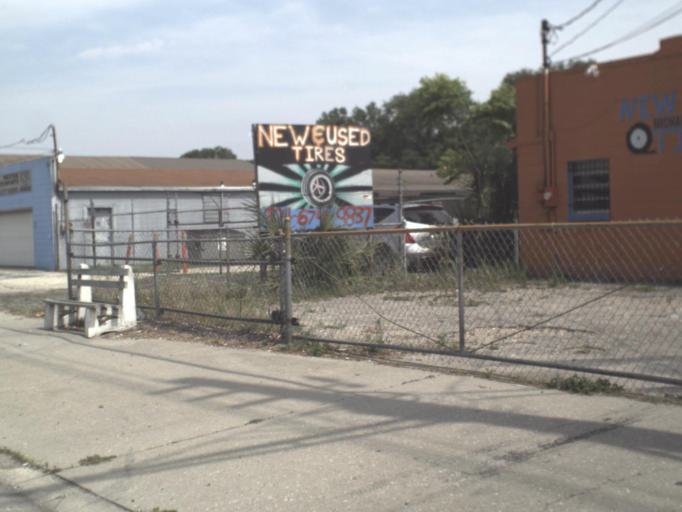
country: US
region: Florida
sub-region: Clay County
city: Bellair-Meadowbrook Terrace
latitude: 30.2480
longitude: -81.7849
